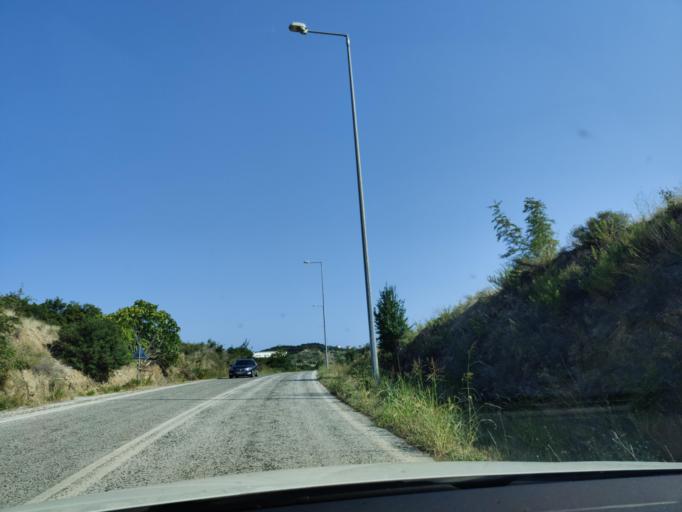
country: GR
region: East Macedonia and Thrace
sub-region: Nomos Kavalas
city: Nea Iraklitsa
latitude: 40.8642
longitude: 24.3006
